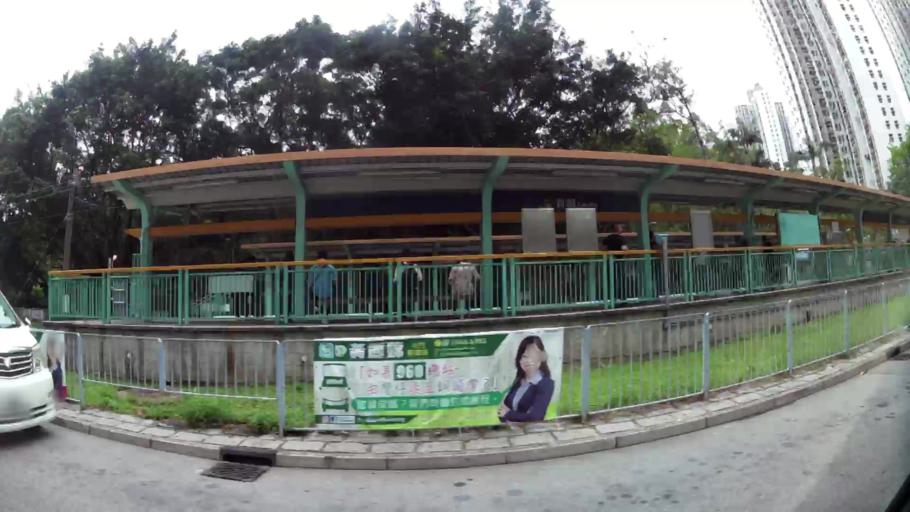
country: HK
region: Tuen Mun
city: Tuen Mun
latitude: 22.4054
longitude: 113.9646
